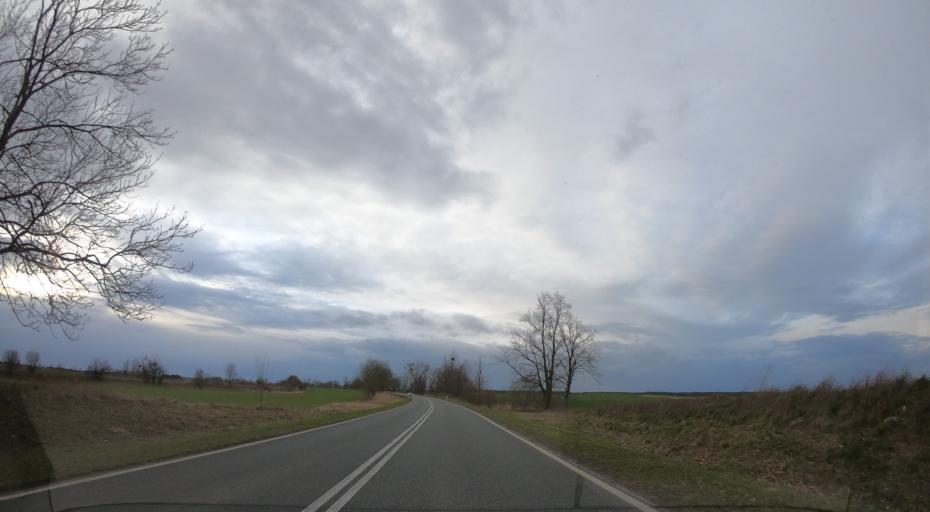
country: PL
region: West Pomeranian Voivodeship
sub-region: Powiat mysliborski
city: Nowogrodek Pomorski
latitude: 52.8995
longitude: 14.9917
